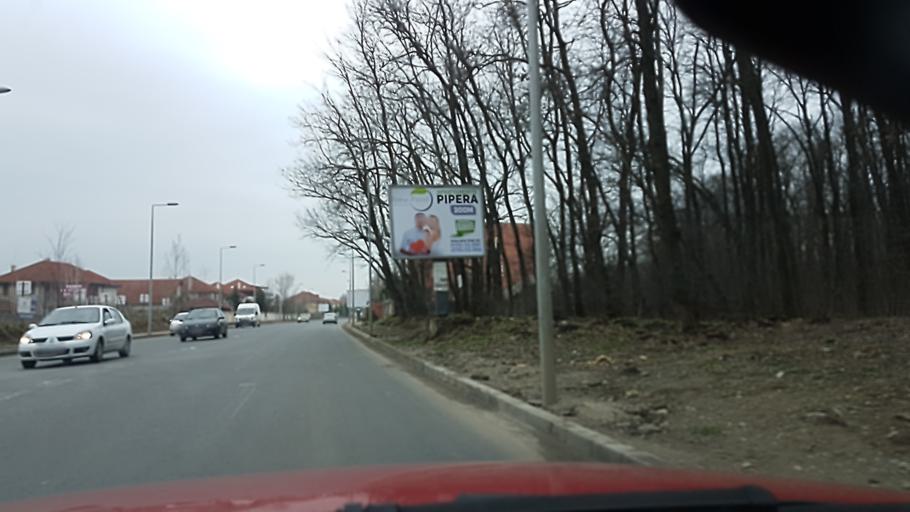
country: RO
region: Ilfov
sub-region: Comuna Tunari
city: Tunari
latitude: 44.5221
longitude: 26.1433
